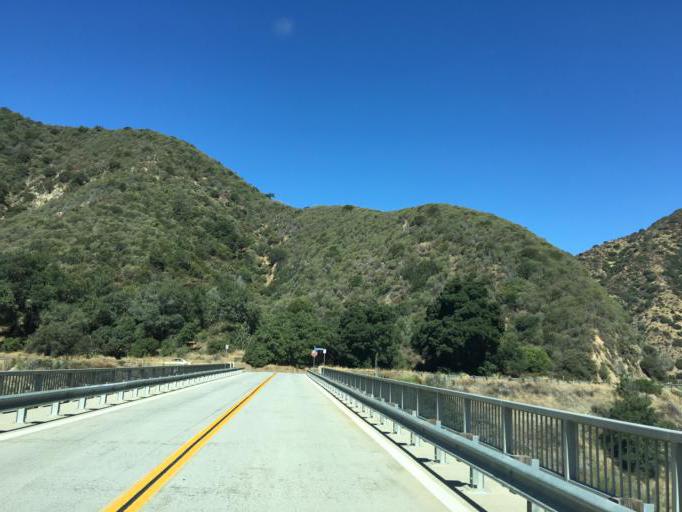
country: US
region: California
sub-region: Los Angeles County
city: Glendora
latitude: 34.2391
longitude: -117.8503
